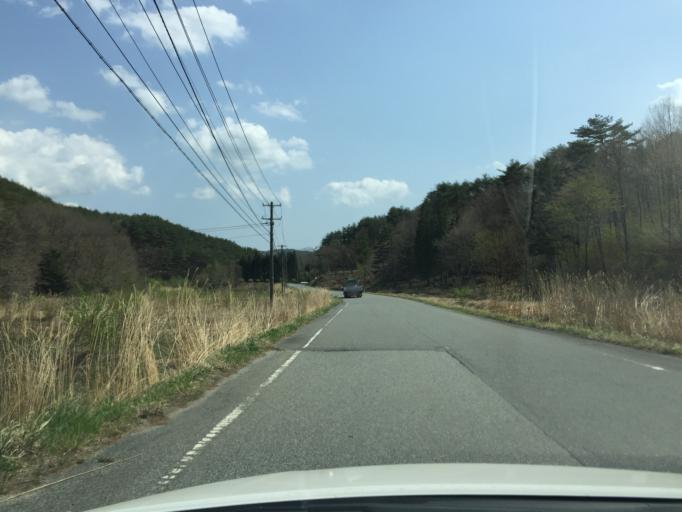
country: JP
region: Fukushima
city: Namie
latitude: 37.3693
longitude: 140.8070
